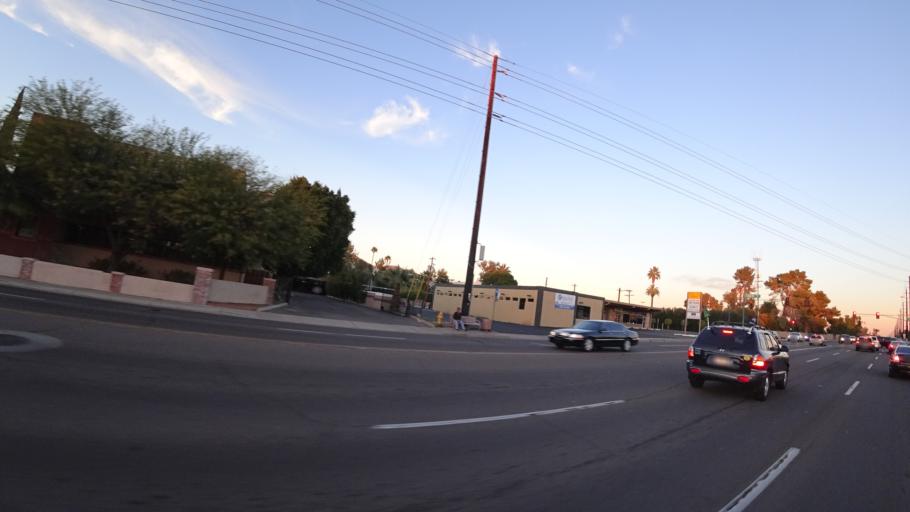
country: US
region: Arizona
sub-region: Maricopa County
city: Paradise Valley
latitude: 33.4800
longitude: -111.9706
